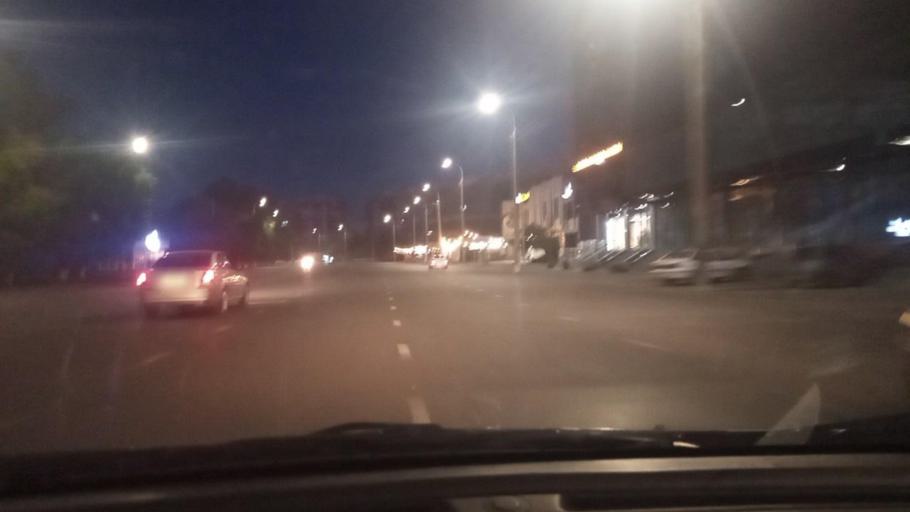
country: UZ
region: Toshkent Shahri
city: Tashkent
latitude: 41.2692
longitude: 69.2588
